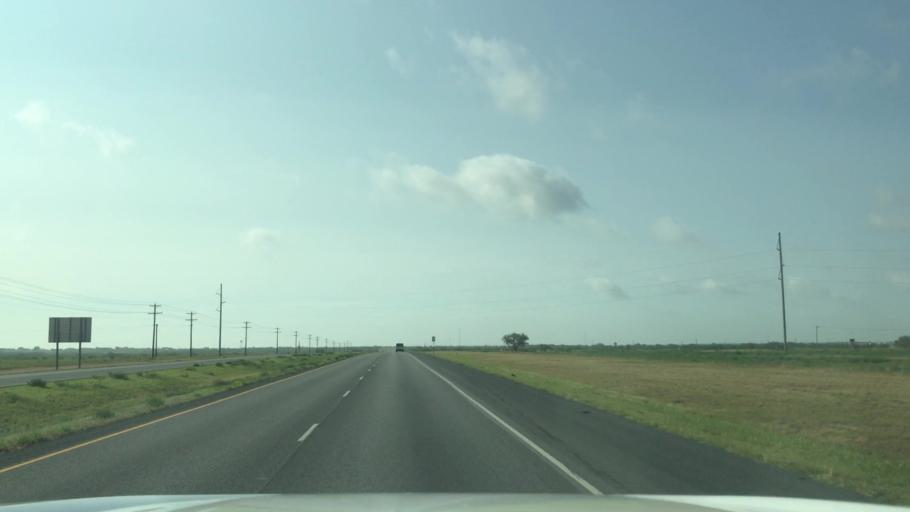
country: US
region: Texas
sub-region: Scurry County
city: Snyder
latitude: 32.7780
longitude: -100.9432
